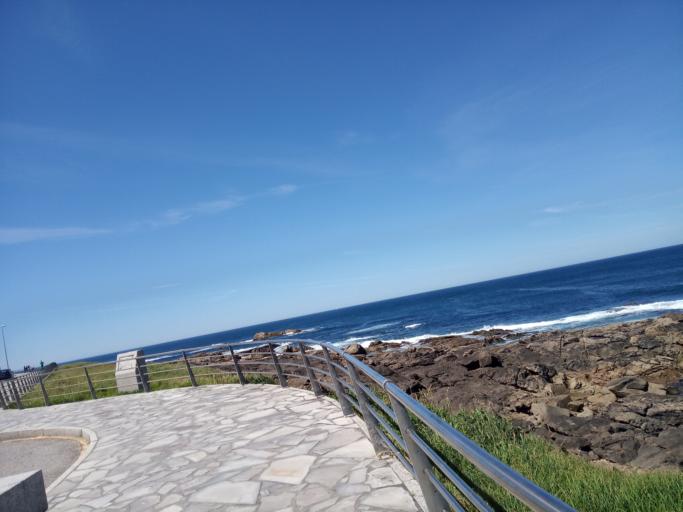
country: ES
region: Galicia
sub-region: Provincia de Pontevedra
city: A Guarda
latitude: 41.8952
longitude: -8.8784
